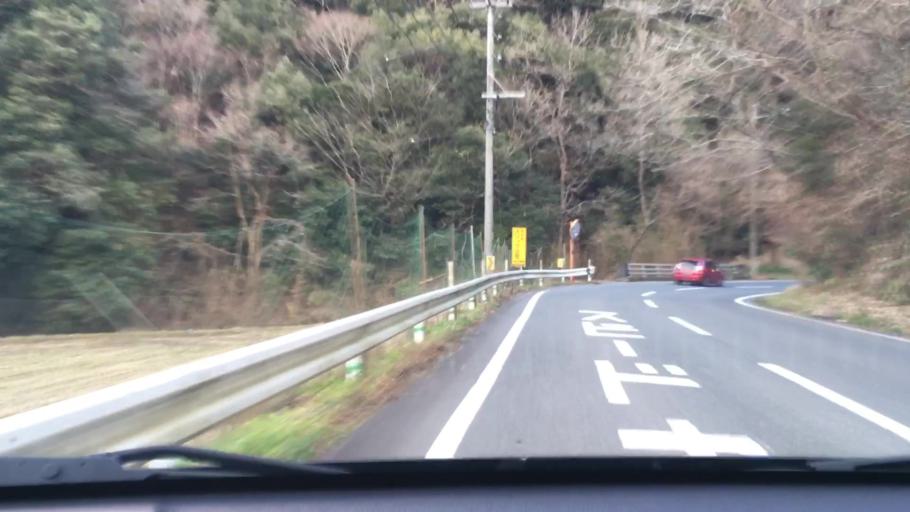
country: JP
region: Oita
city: Bungo-Takada-shi
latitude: 33.4622
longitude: 131.3889
